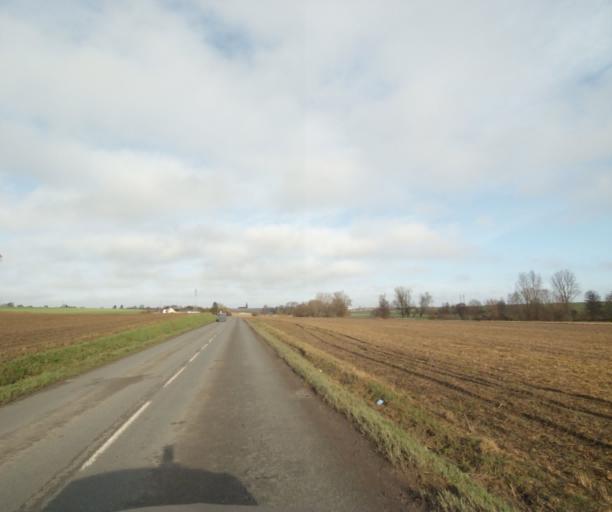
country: FR
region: Nord-Pas-de-Calais
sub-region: Departement du Nord
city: Thiant
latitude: 50.2909
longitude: 3.4484
